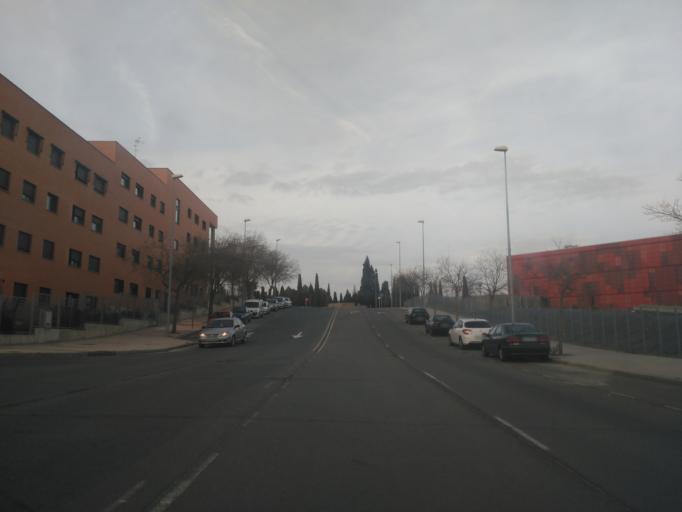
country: ES
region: Castille and Leon
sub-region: Provincia de Salamanca
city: Salamanca
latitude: 40.9691
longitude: -5.6838
